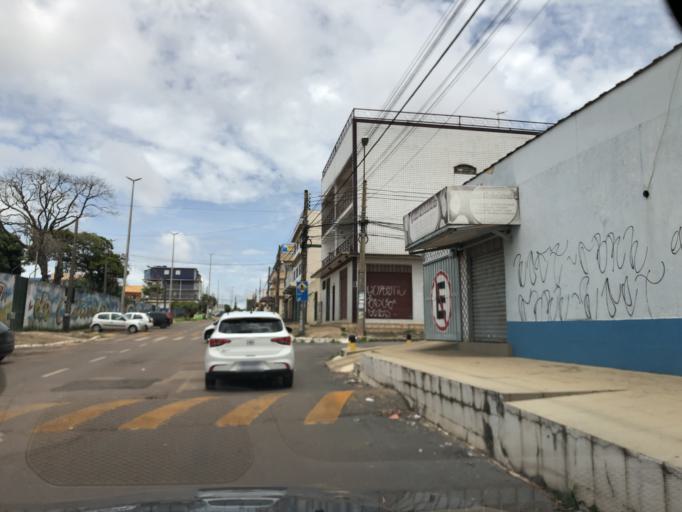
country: BR
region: Federal District
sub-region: Brasilia
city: Brasilia
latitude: -15.8177
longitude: -48.0984
